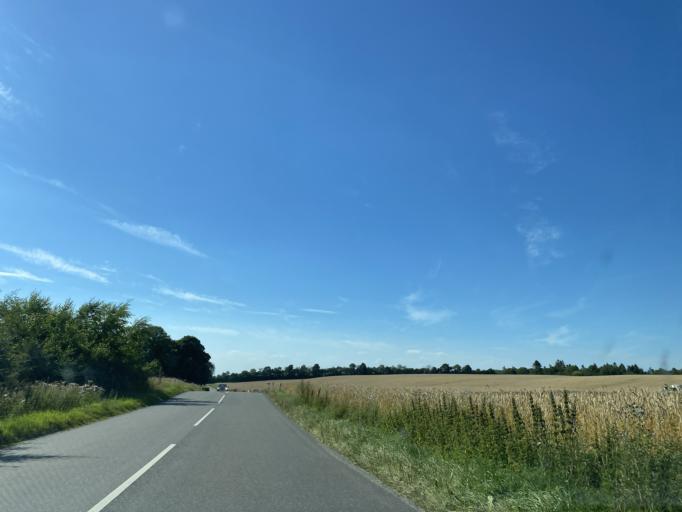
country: DK
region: South Denmark
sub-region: Vejle Kommune
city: Give
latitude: 55.8722
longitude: 9.3407
